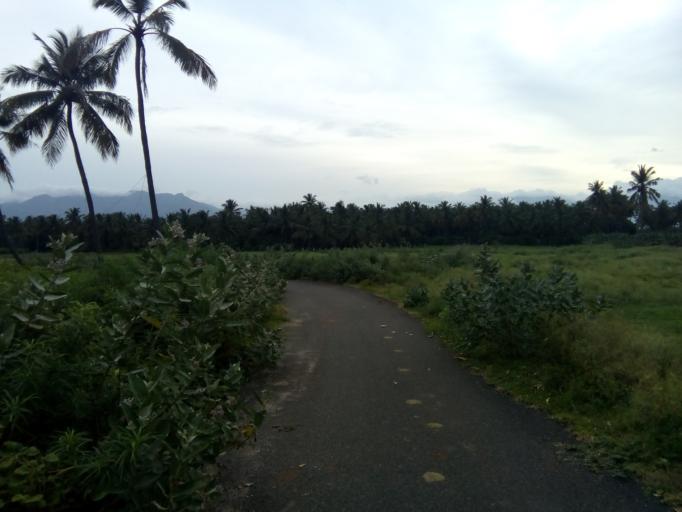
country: IN
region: Tamil Nadu
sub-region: Coimbatore
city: Perur
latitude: 10.9946
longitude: 76.8522
